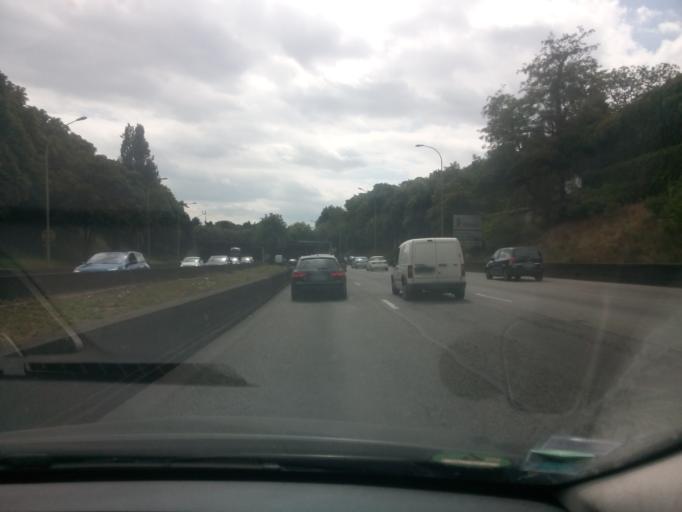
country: FR
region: Ile-de-France
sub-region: Departement du Val-de-Marne
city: Saint-Mande
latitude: 48.8336
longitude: 2.4091
